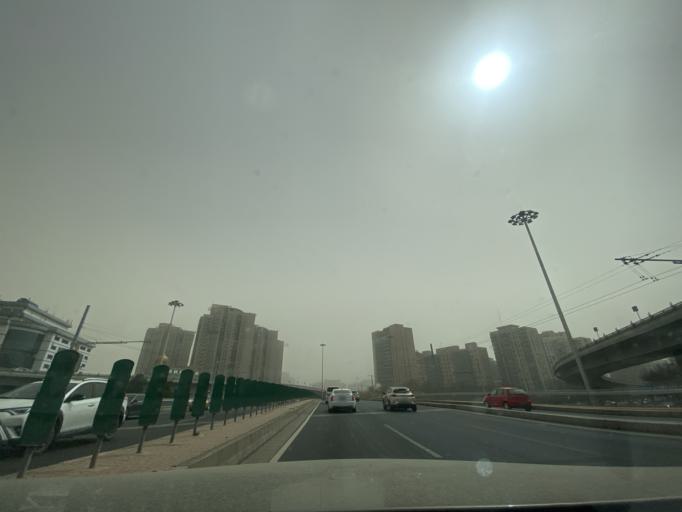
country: CN
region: Beijing
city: Sijiqing
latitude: 39.9412
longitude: 116.3033
